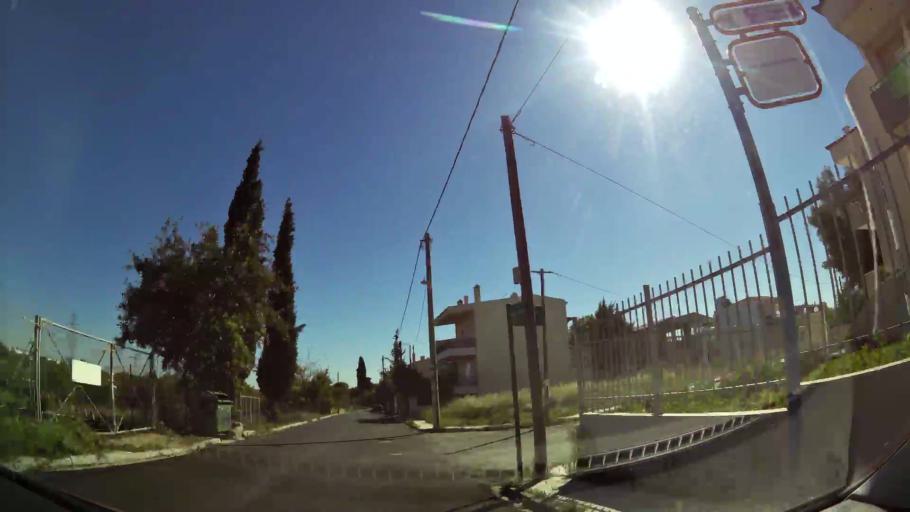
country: GR
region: Attica
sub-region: Nomarchia Anatolikis Attikis
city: Leondarion
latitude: 37.9926
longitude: 23.8623
